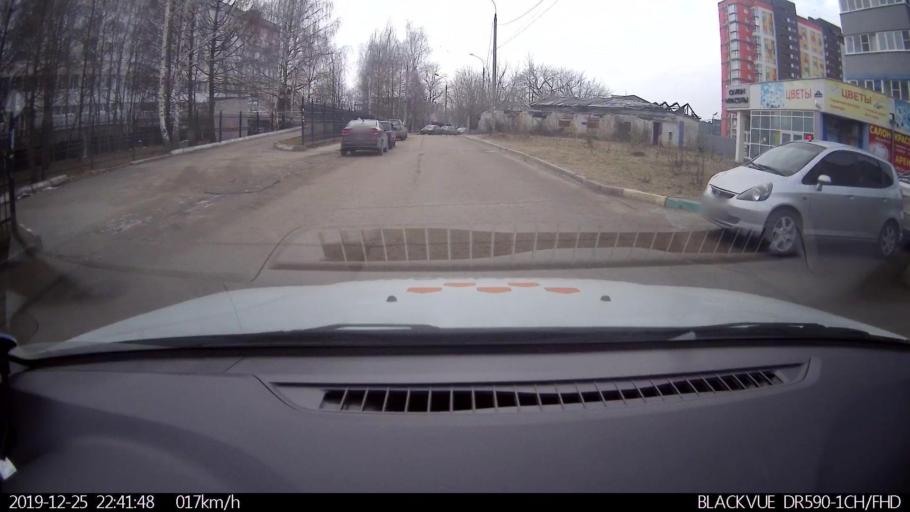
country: RU
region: Nizjnij Novgorod
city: Gorbatovka
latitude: 56.2340
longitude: 43.8431
